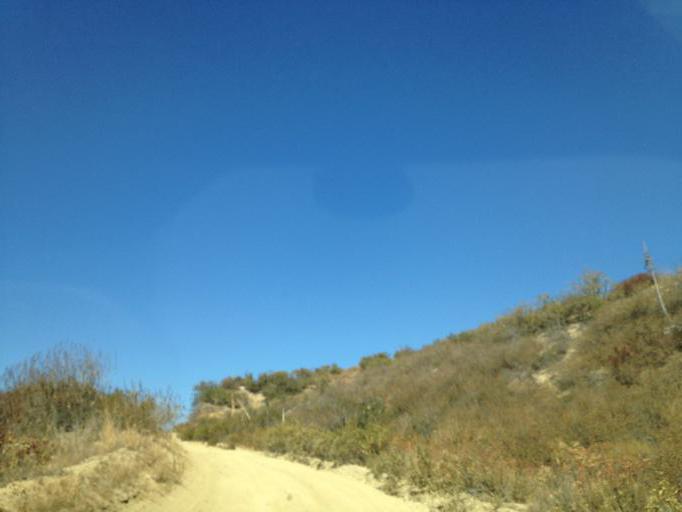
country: US
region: California
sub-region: San Bernardino County
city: Mentone
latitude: 34.1240
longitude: -117.1097
